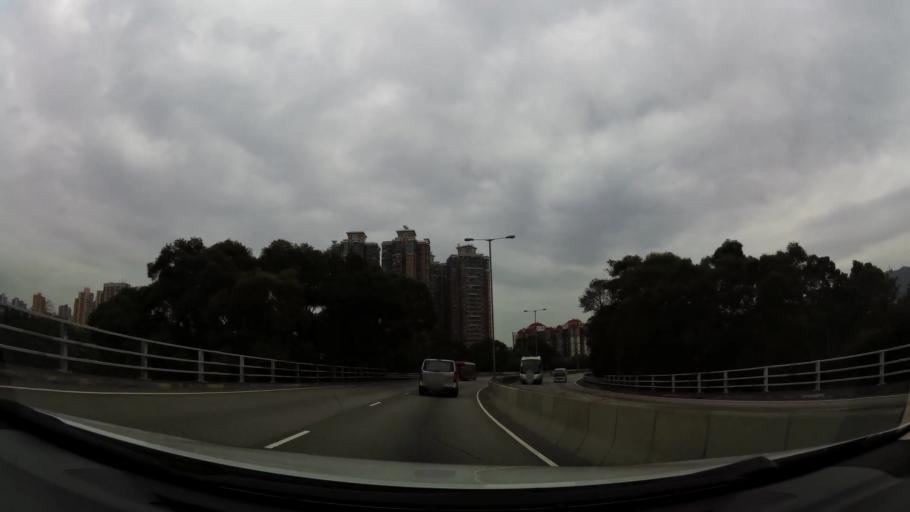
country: HK
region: Yuen Long
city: Yuen Long Kau Hui
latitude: 22.4464
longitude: 114.0162
